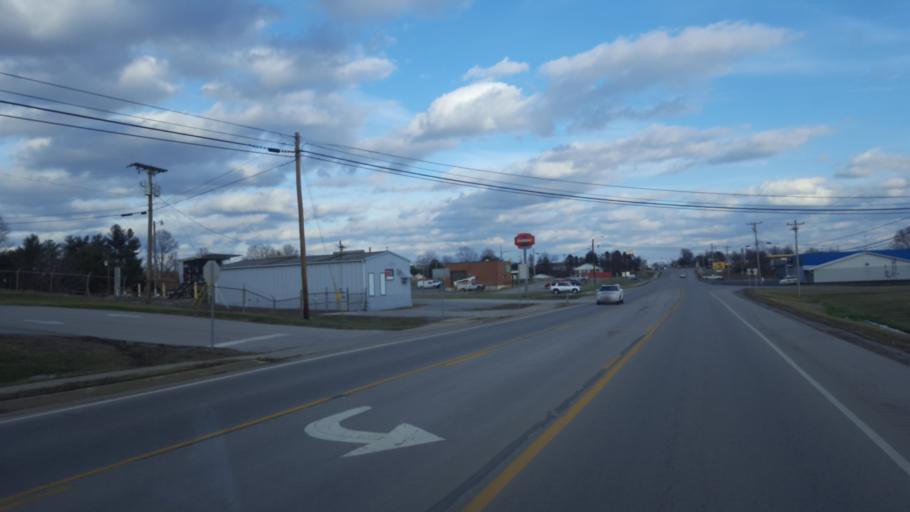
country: US
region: Kentucky
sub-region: Fleming County
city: Flemingsburg
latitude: 38.4205
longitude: -83.7590
